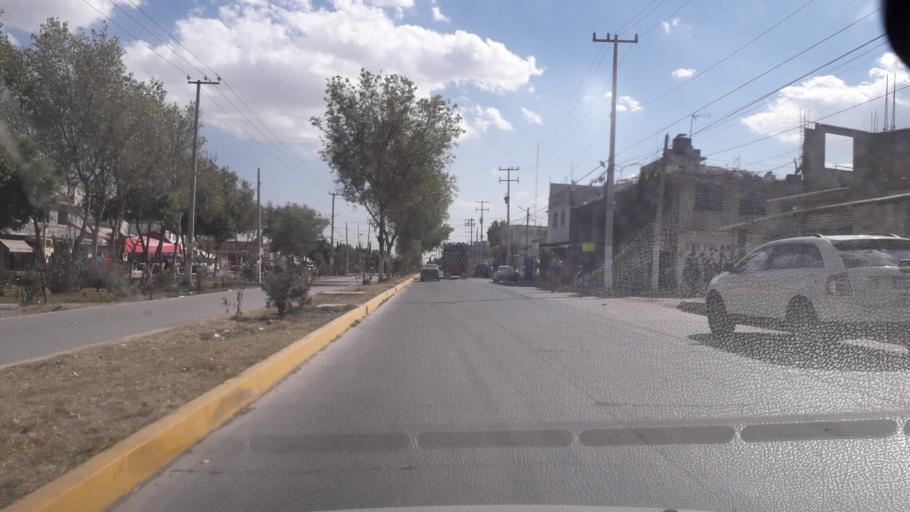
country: MX
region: Mexico
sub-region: Jaltenco
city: Alborada Jaltenco
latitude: 19.6421
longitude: -99.0593
